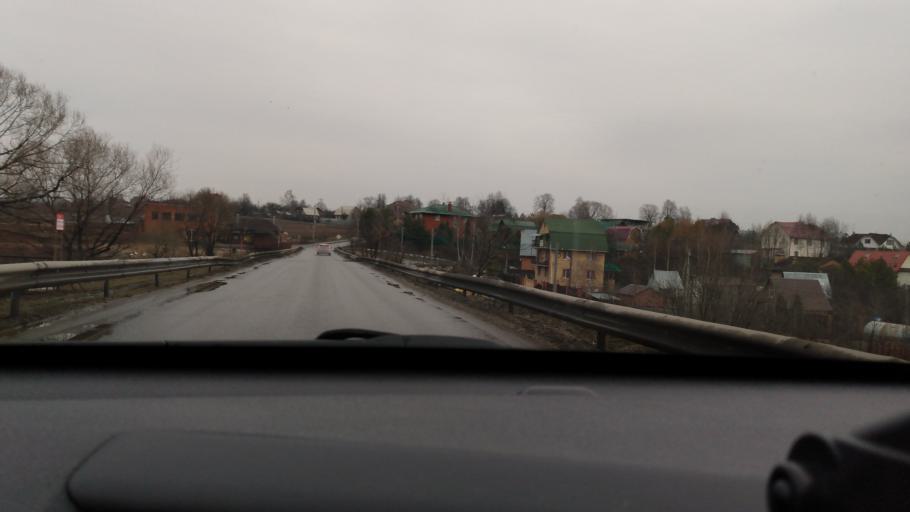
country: RU
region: Moscow
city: Zagor'ye
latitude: 55.5534
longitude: 37.6630
